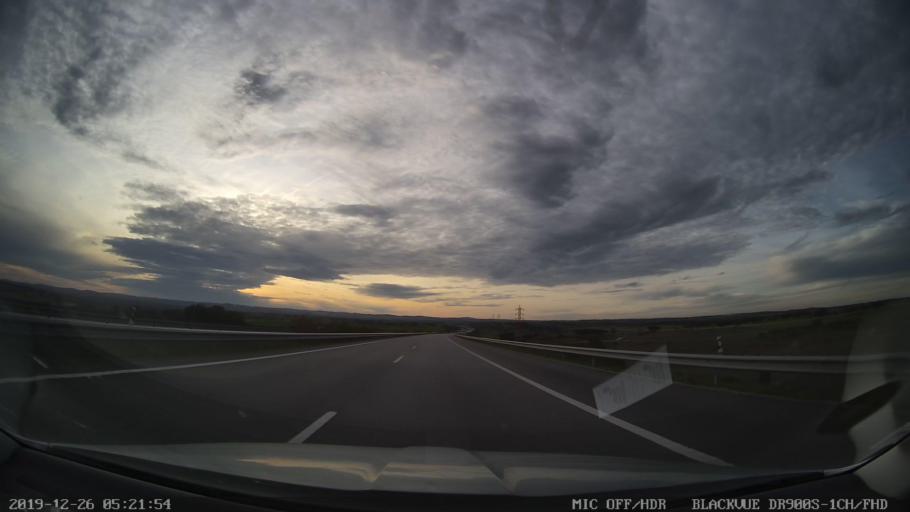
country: PT
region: Evora
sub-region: Vila Vicosa
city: Vila Vicosa
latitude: 38.8501
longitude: -7.3476
